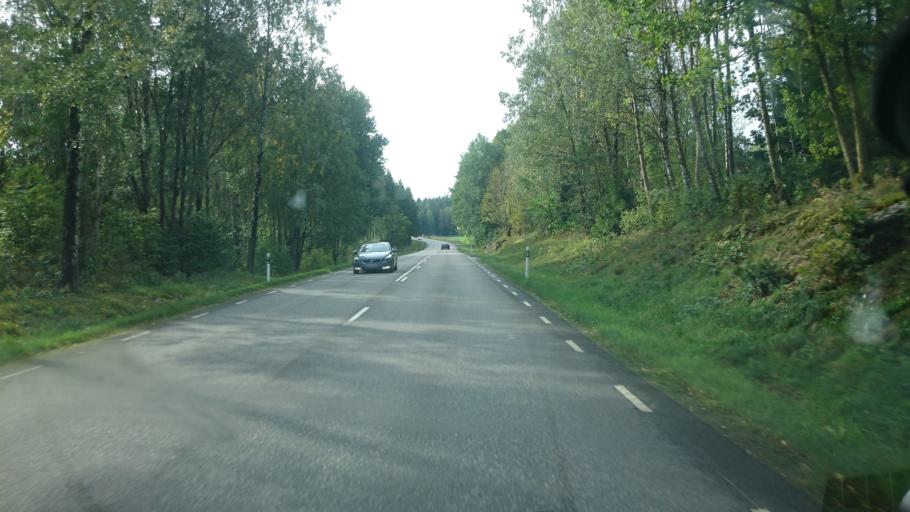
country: SE
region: Vaestra Goetaland
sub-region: Alingsas Kommun
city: Alingsas
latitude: 58.0112
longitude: 12.4479
